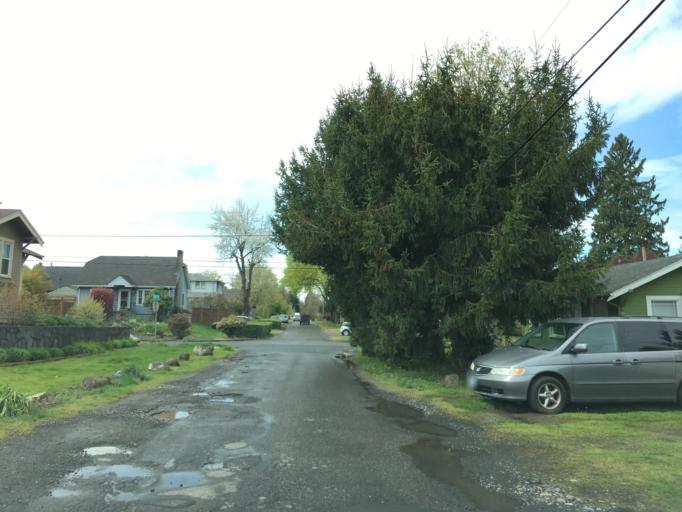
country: US
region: Oregon
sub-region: Multnomah County
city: Lents
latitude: 45.5496
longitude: -122.5897
